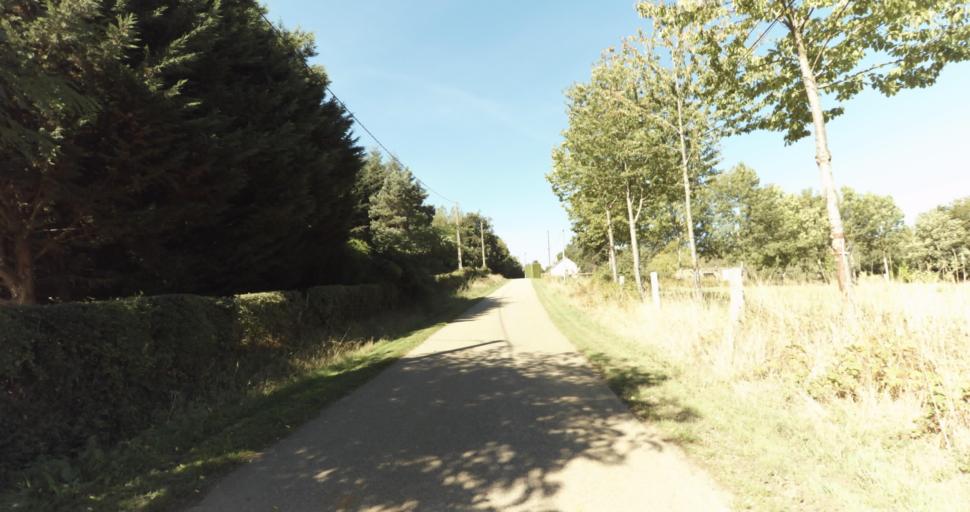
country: FR
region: Lower Normandy
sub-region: Departement de l'Orne
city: Gace
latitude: 48.7832
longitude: 0.2729
